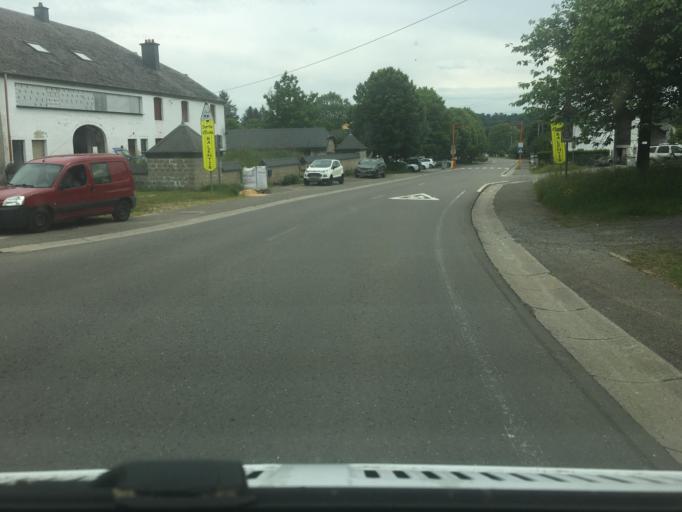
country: BE
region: Wallonia
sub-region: Province du Luxembourg
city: Florenville
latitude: 49.7151
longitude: 5.3194
